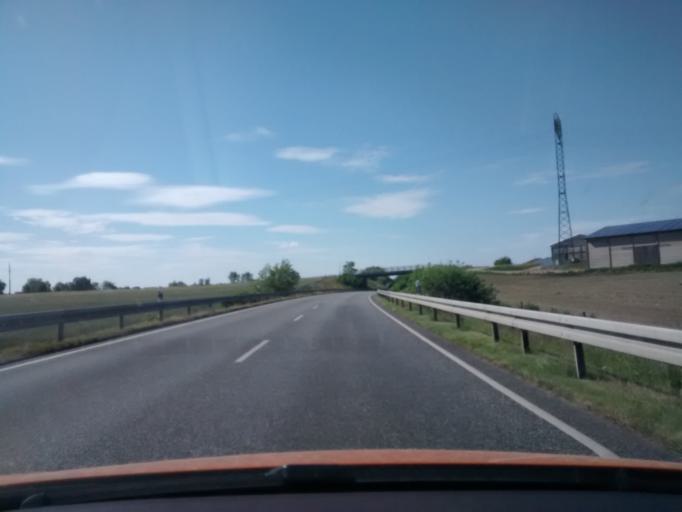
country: DE
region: Brandenburg
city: Juterbog
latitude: 52.0041
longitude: 13.1002
